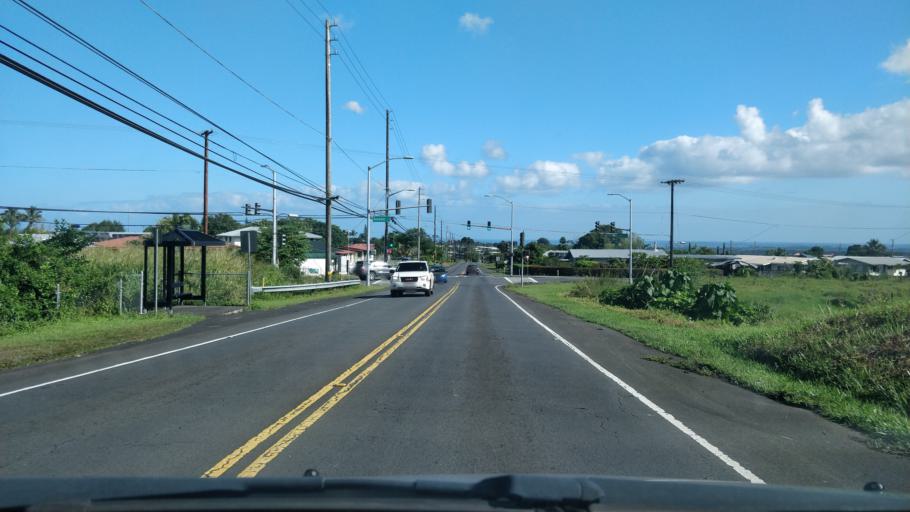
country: US
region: Hawaii
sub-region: Hawaii County
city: Hilo
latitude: 19.6722
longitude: -155.0929
